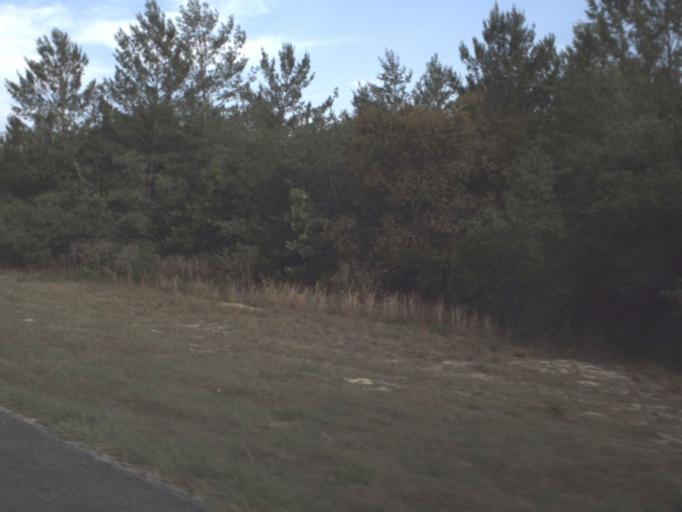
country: US
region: Florida
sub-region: Marion County
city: Silver Springs Shores
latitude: 29.1770
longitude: -81.7858
